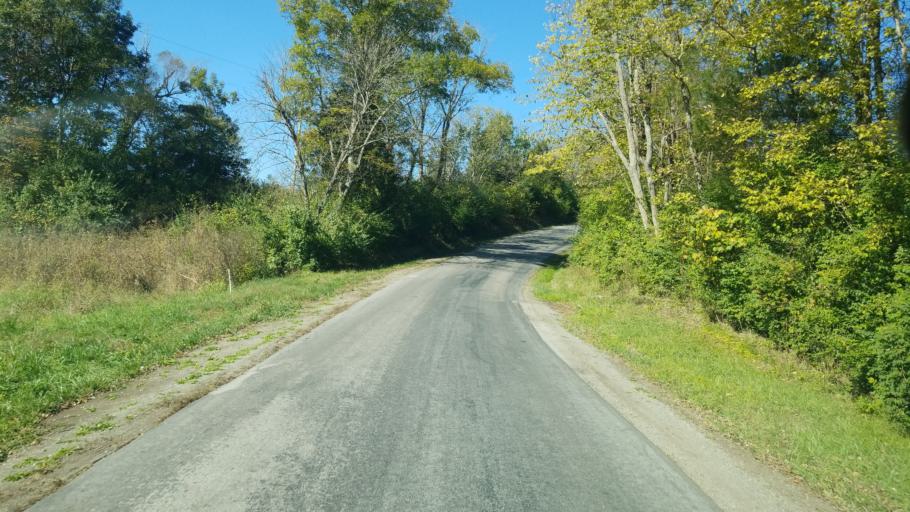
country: US
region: Ohio
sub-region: Highland County
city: Leesburg
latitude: 39.2791
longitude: -83.4723
